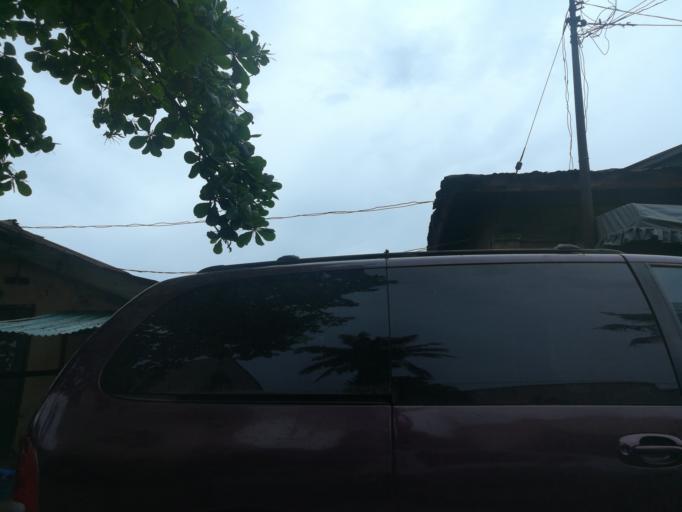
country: NG
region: Lagos
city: Ebute Metta
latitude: 6.4881
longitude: 3.3867
